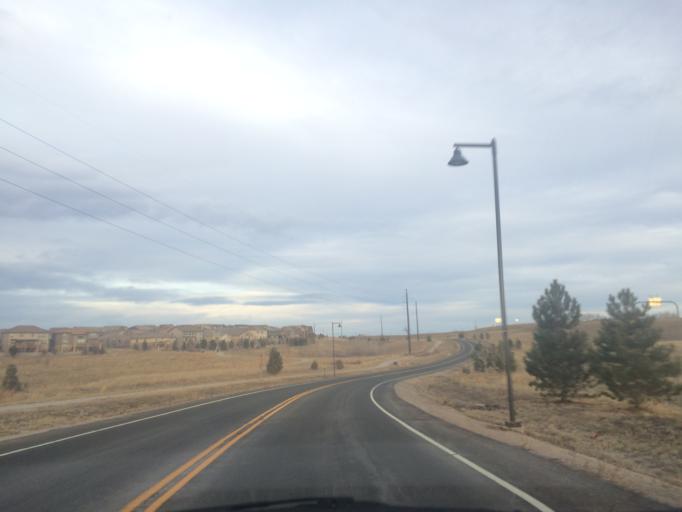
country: US
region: Colorado
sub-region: Boulder County
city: Lafayette
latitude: 39.9834
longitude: -105.0340
